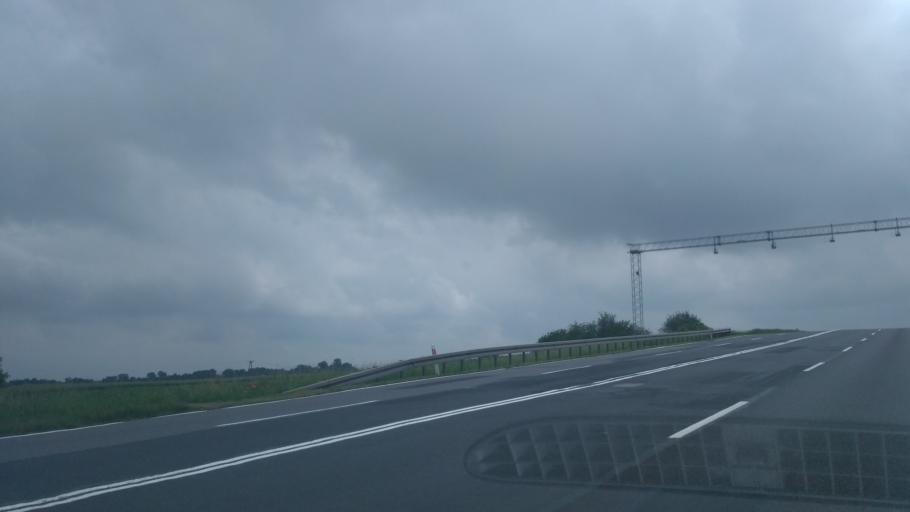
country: PL
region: Subcarpathian Voivodeship
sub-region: Powiat przeworski
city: Rozborz
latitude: 50.0490
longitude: 22.5317
